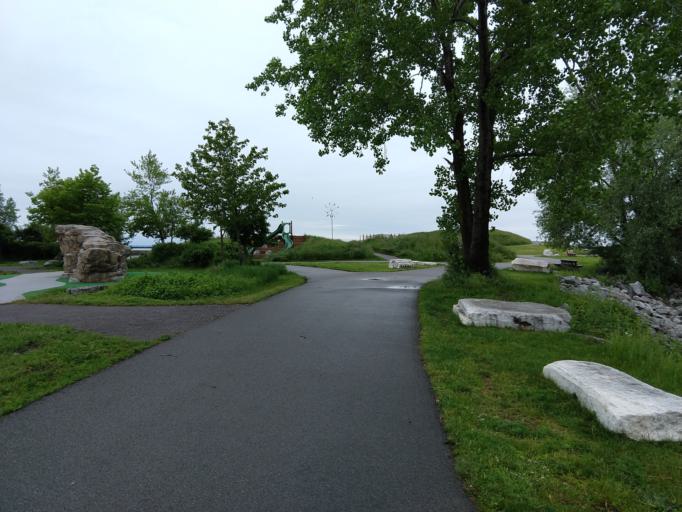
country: US
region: New York
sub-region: Erie County
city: Buffalo
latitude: 42.8709
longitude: -78.8833
